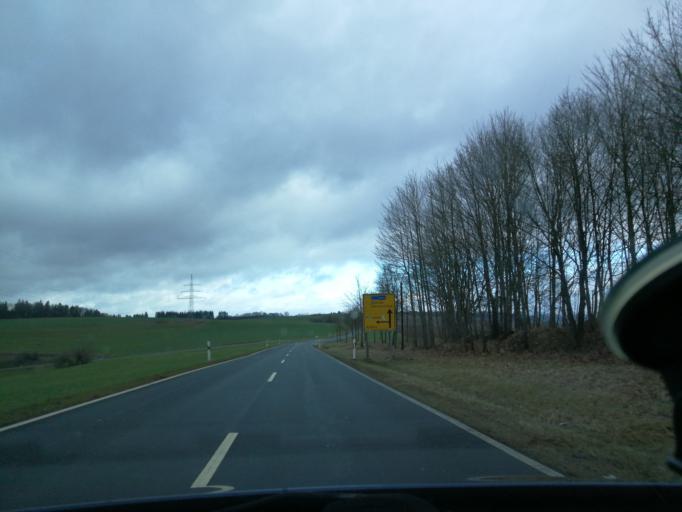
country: DE
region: Rheinland-Pfalz
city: Nohn
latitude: 50.3378
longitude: 6.7844
